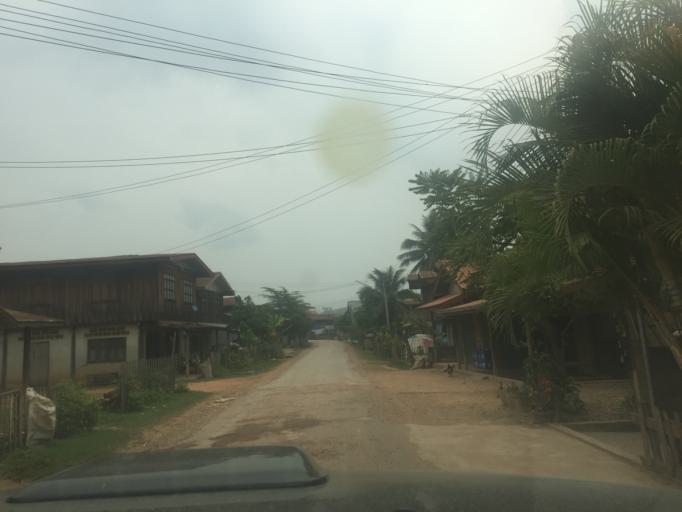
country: LA
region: Vientiane
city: Muang Sanakham
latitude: 18.4035
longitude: 101.5029
